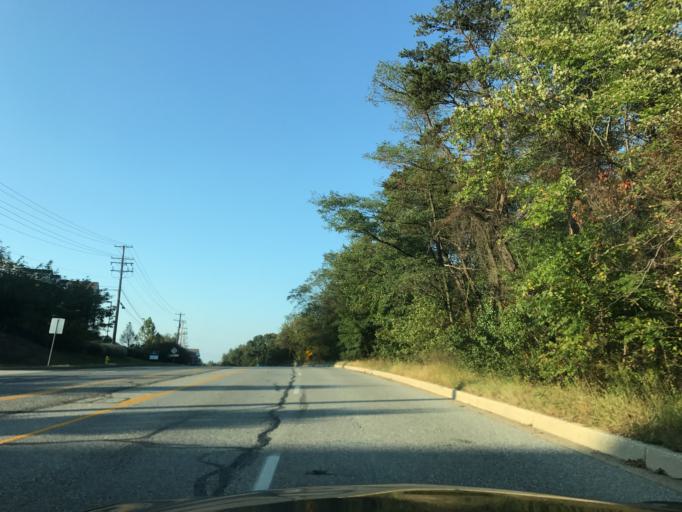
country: US
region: Maryland
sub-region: Anne Arundel County
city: South Gate
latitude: 39.0880
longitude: -76.6233
